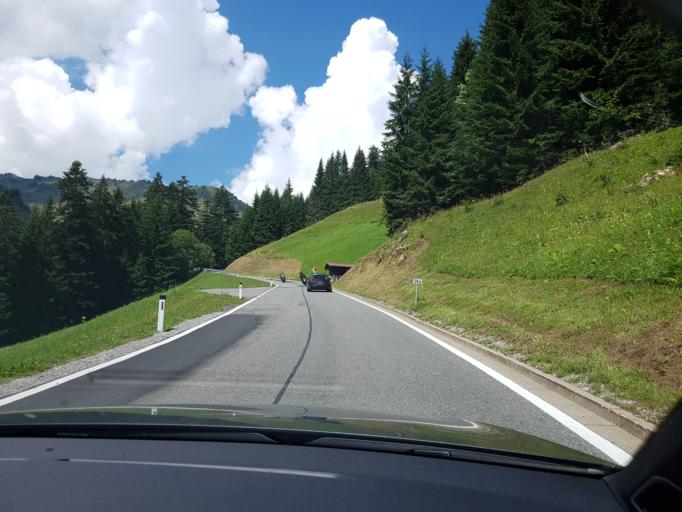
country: AT
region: Vorarlberg
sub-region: Politischer Bezirk Bregenz
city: Damuels
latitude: 47.2600
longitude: 9.9140
